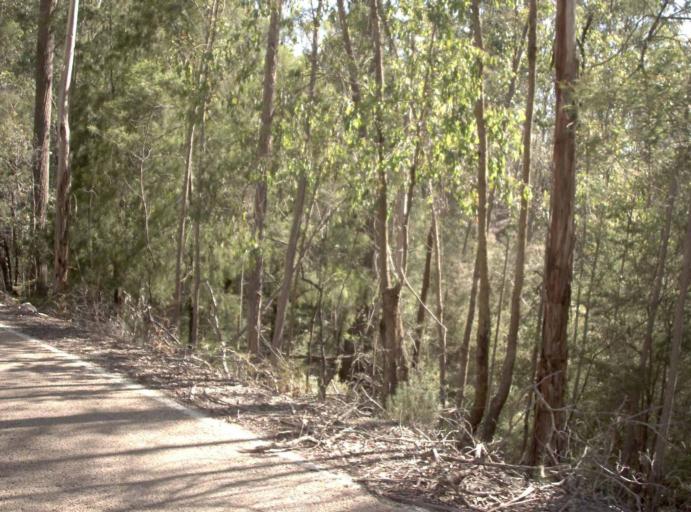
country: AU
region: Victoria
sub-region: East Gippsland
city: Lakes Entrance
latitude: -37.4984
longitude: 148.5518
